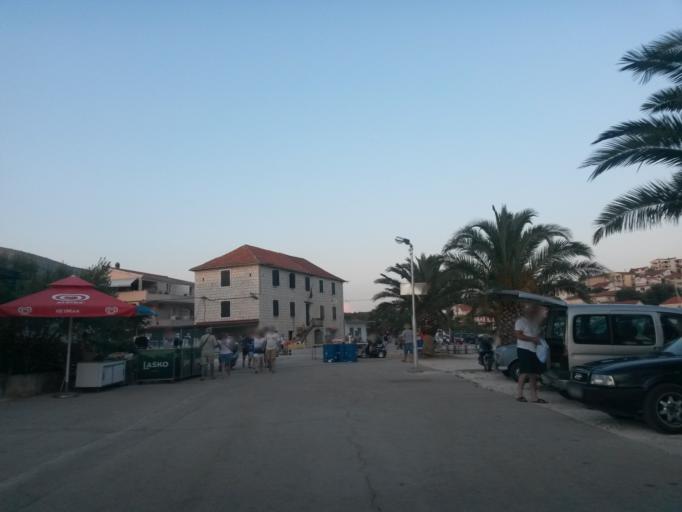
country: HR
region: Splitsko-Dalmatinska
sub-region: Grad Trogir
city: Trogir
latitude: 43.5116
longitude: 16.1834
